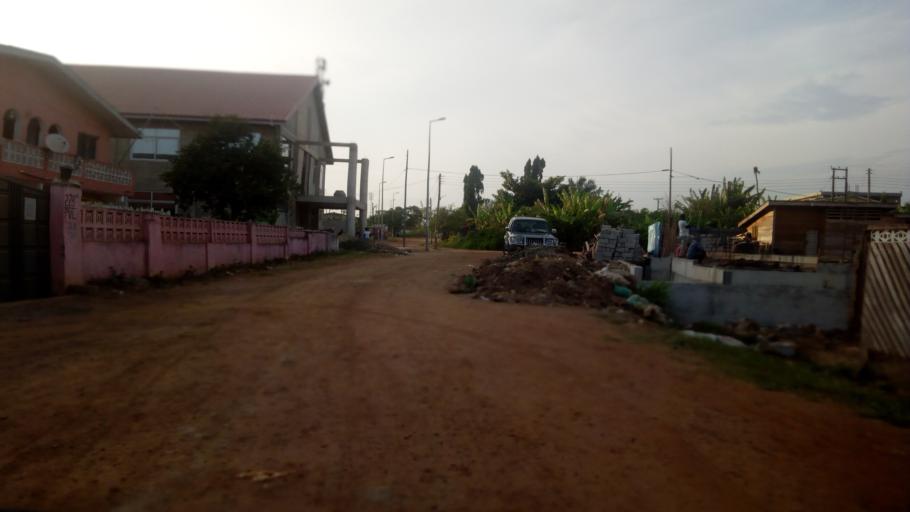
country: GH
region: Central
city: Cape Coast
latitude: 5.1289
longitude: -1.2761
